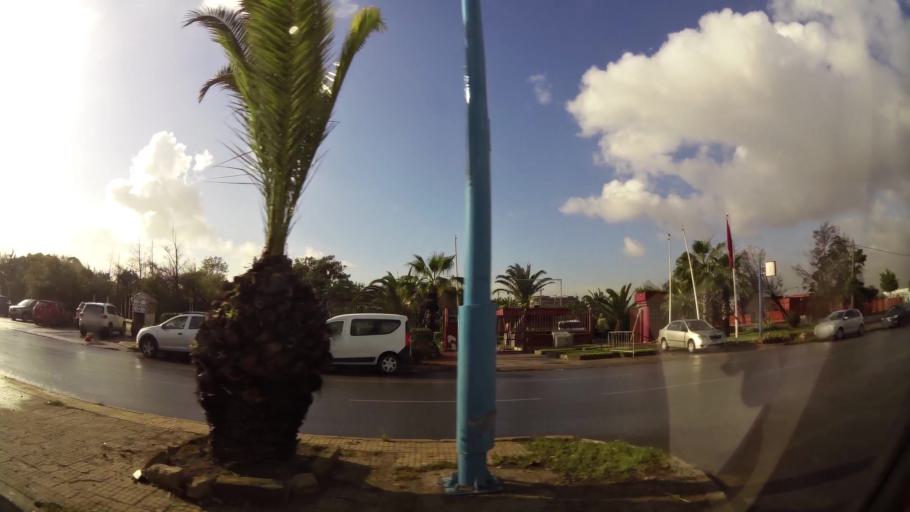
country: MA
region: Grand Casablanca
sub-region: Mediouna
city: Tit Mellil
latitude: 33.5953
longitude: -7.5274
